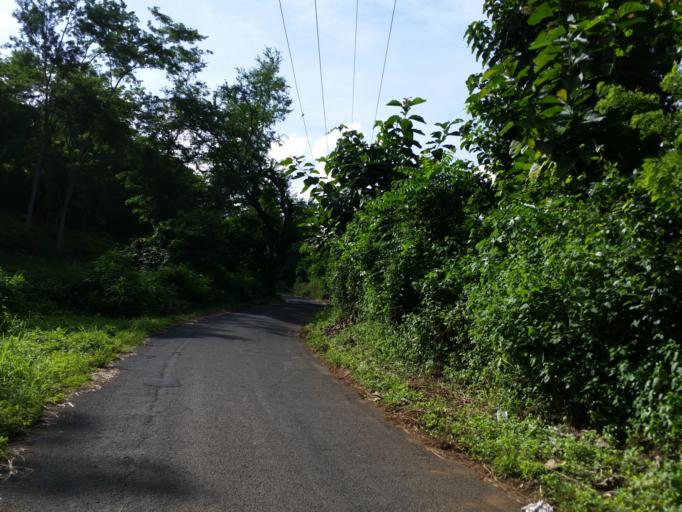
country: NI
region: Managua
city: Managua
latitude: 12.0681
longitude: -86.2558
